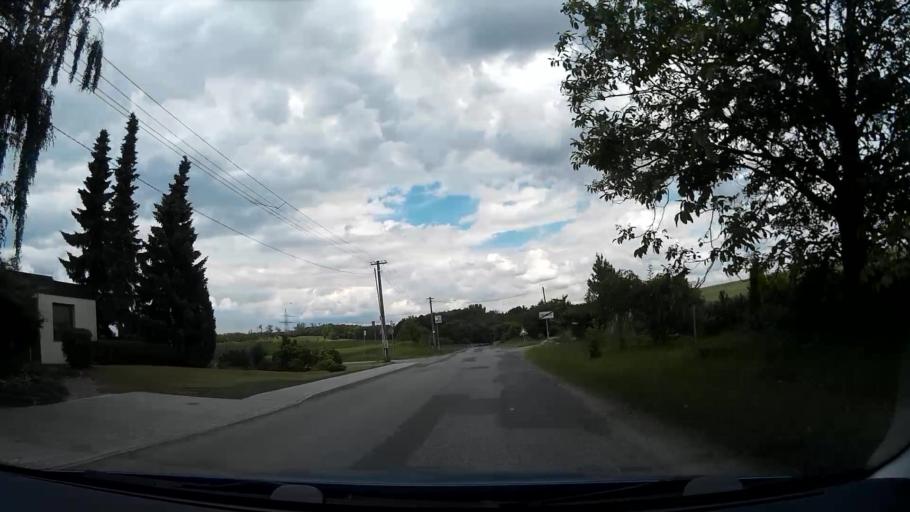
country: CZ
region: South Moravian
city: Orechov
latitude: 49.1193
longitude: 16.5262
